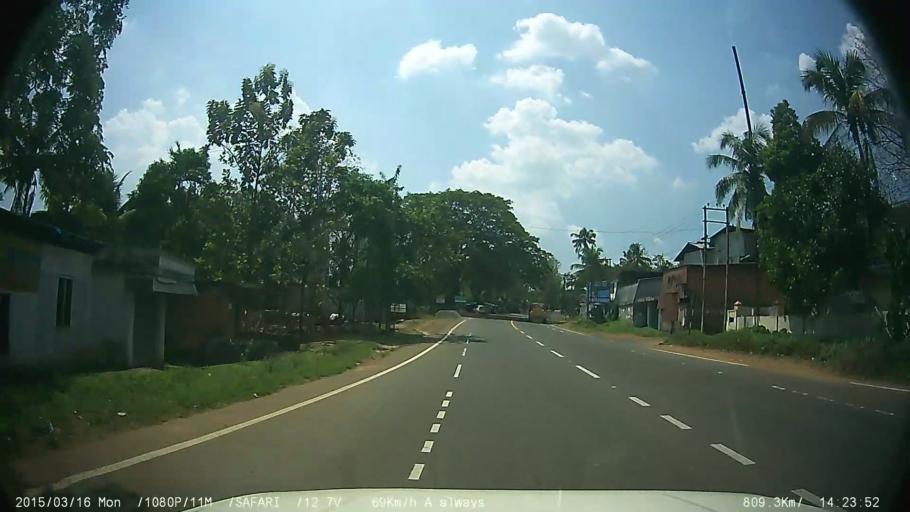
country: IN
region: Kerala
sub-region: Ernakulam
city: Perumbavoor
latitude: 10.0710
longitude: 76.5122
